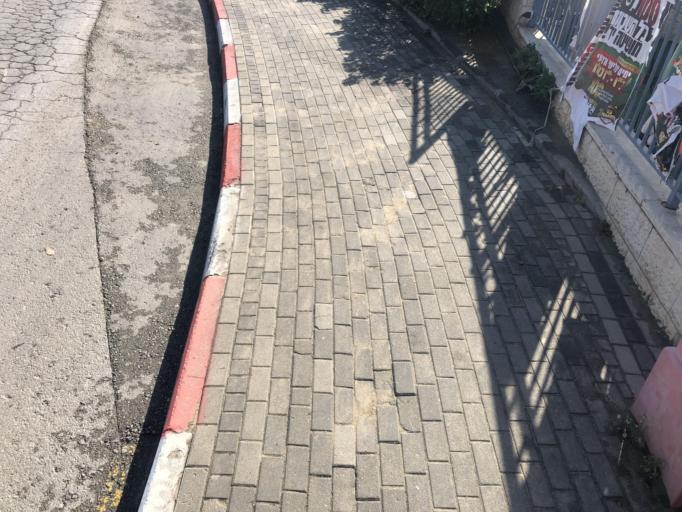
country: IL
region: Jerusalem
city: Modiin Ilit
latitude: 31.9242
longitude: 35.0475
